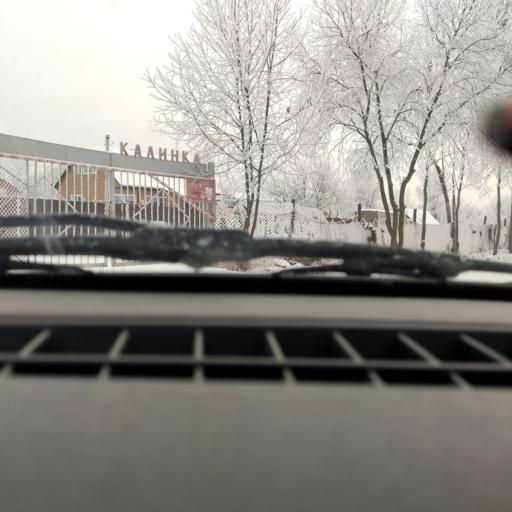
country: RU
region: Bashkortostan
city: Ufa
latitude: 54.7162
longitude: 56.1340
